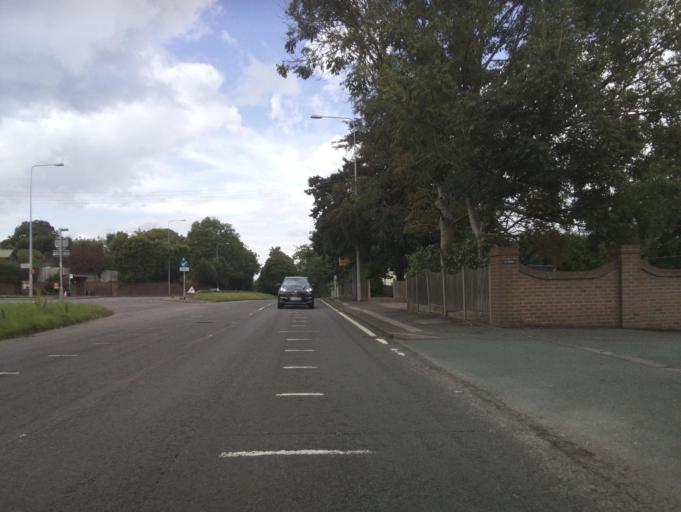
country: GB
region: England
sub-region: Staffordshire
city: Barlaston
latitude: 52.9434
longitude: -2.1893
